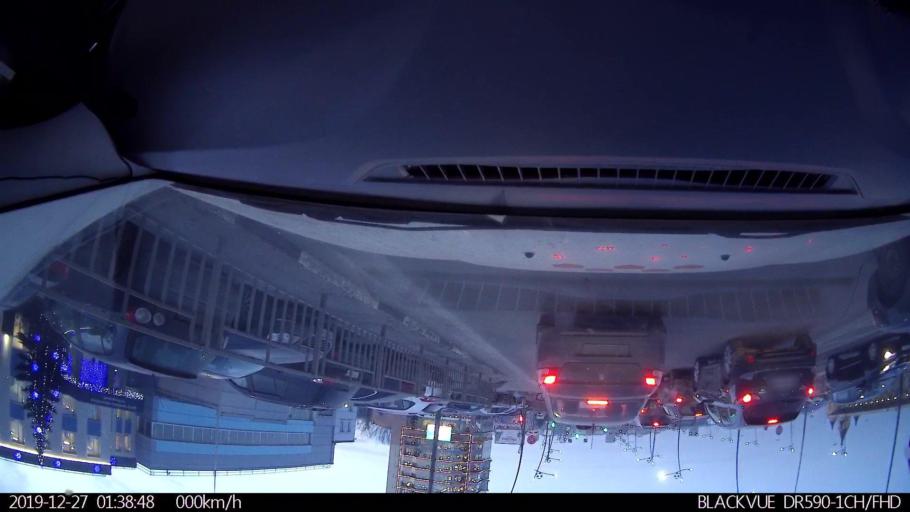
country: RU
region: Nizjnij Novgorod
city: Nizhniy Novgorod
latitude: 56.3341
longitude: 43.9614
